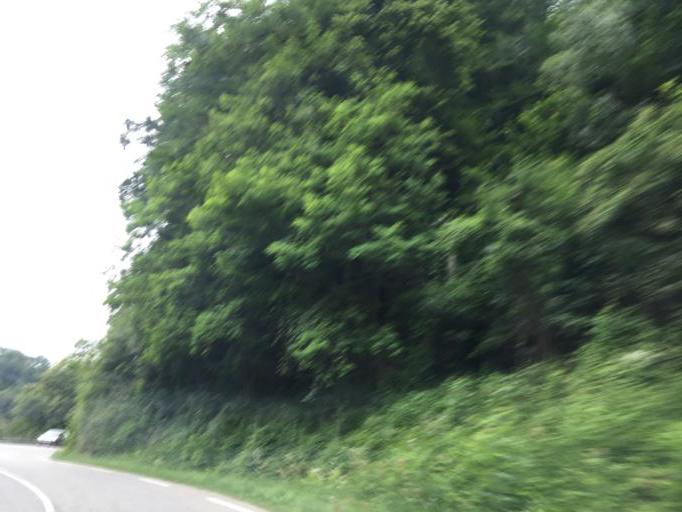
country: FR
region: Rhone-Alpes
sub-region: Departement de la Savoie
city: Saint-Beron
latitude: 45.4829
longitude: 5.7224
